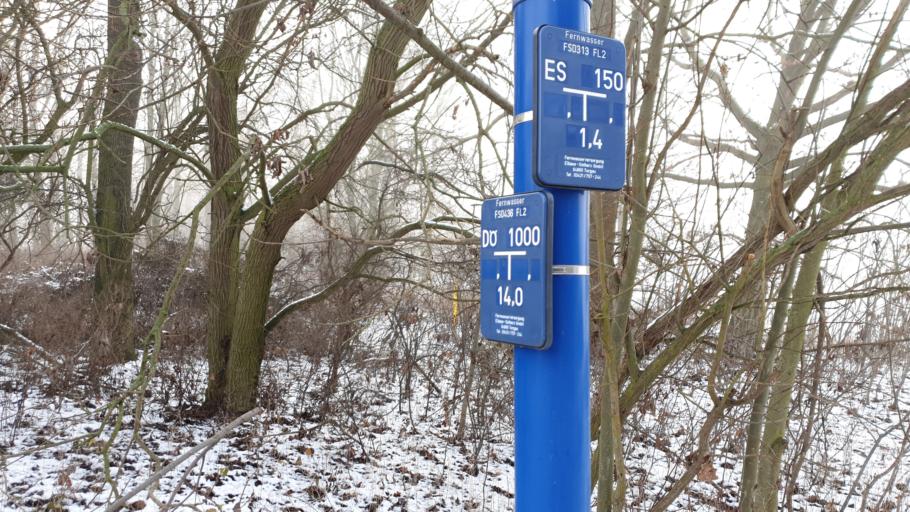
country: DE
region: Saxony
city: Taucha
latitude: 51.3976
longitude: 12.4901
